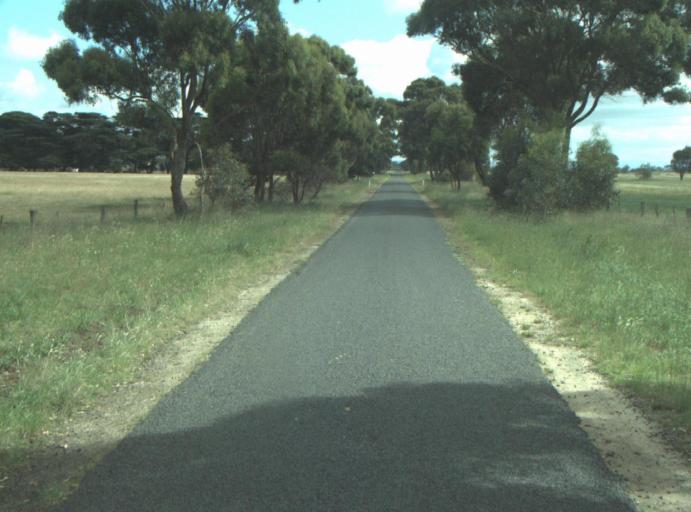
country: AU
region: Victoria
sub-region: Greater Geelong
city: Lara
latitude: -37.8675
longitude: 144.3506
